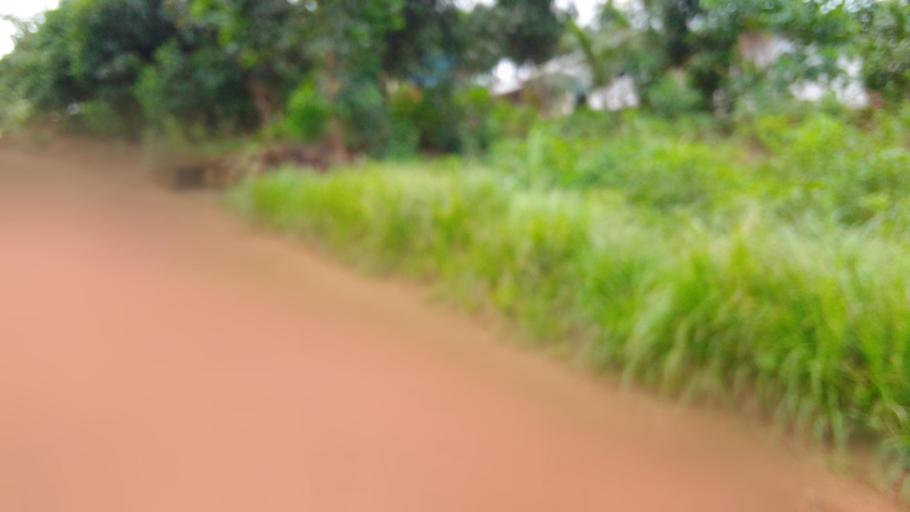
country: SL
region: Eastern Province
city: Kenema
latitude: 7.8503
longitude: -11.1856
